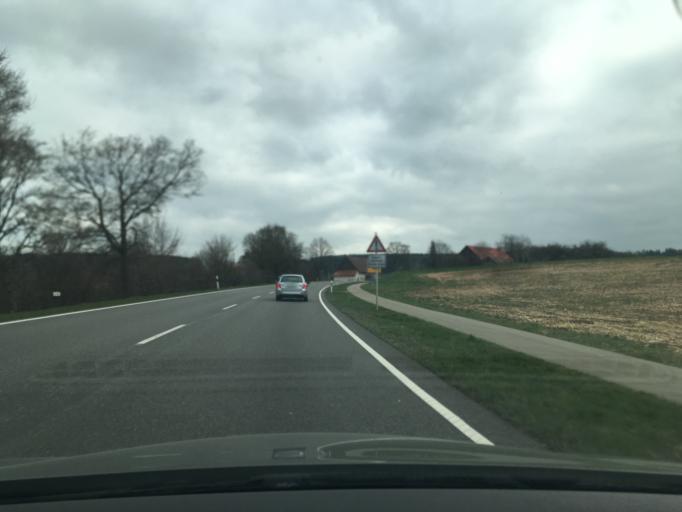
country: DE
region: Baden-Wuerttemberg
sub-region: Tuebingen Region
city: Eberhardzell
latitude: 47.9796
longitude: 9.7764
